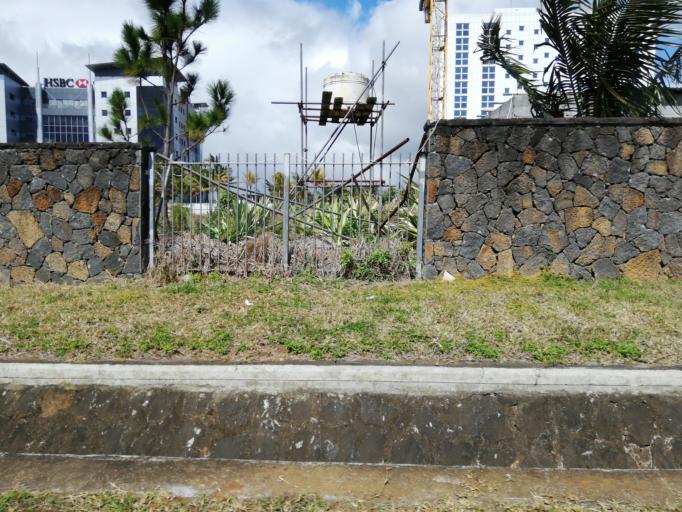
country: MU
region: Plaines Wilhems
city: Ebene
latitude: -20.2437
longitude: 57.4947
